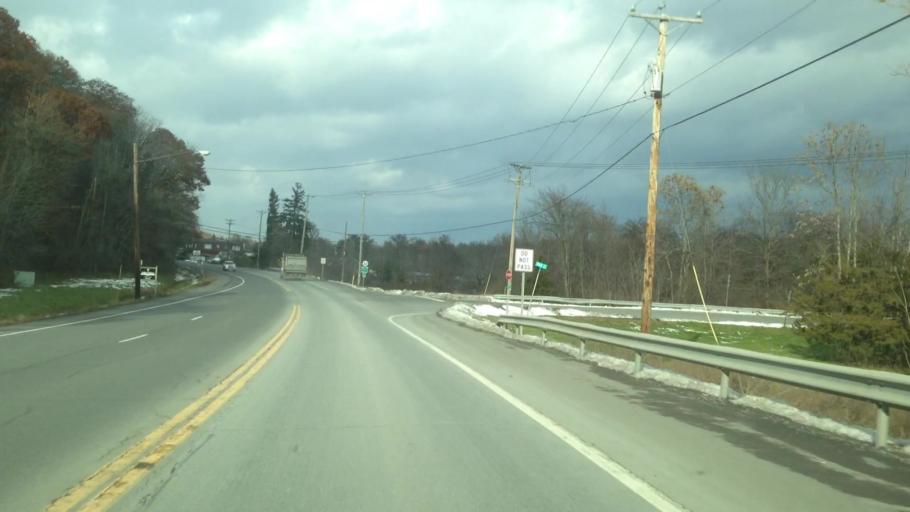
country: US
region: New York
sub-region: Ulster County
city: Lincoln Park
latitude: 41.9619
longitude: -73.9706
